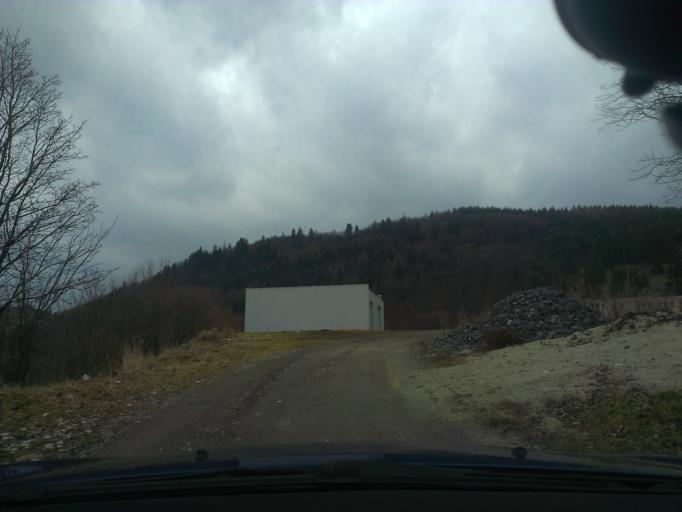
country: SK
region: Banskobystricky
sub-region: Okres Banska Bystrica
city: Banska Stiavnica
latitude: 48.4480
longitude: 18.8747
